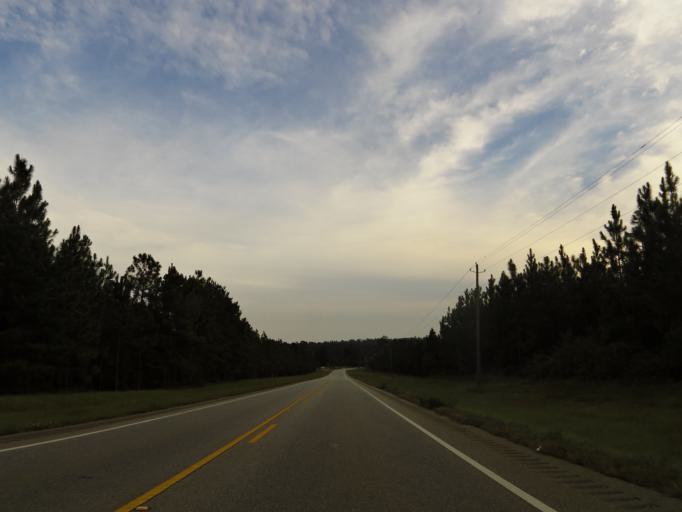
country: US
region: Alabama
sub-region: Monroe County
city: Frisco City
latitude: 31.2632
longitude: -87.4961
